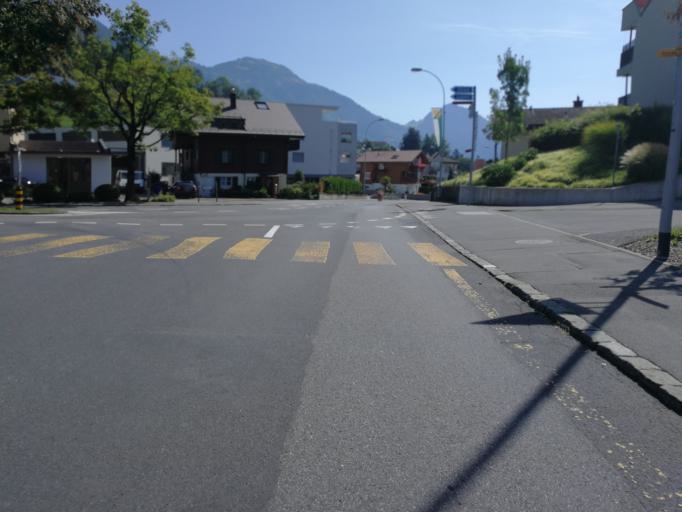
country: CH
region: Lucerne
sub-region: Lucerne-Land District
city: Weggis
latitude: 47.0350
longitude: 8.4234
